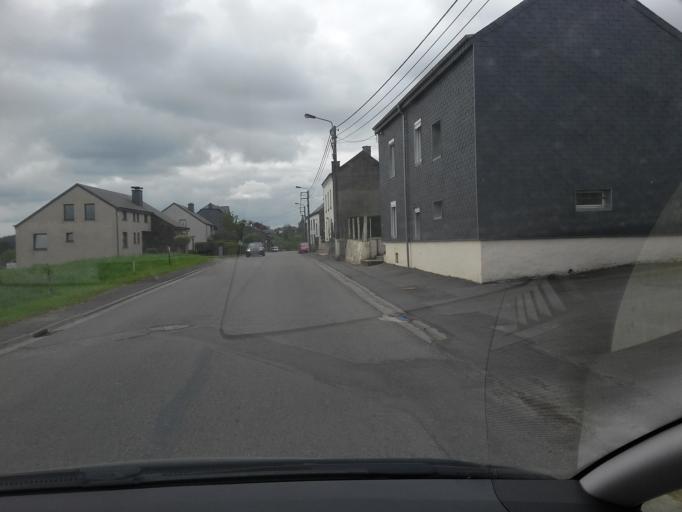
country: BE
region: Wallonia
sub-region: Province du Luxembourg
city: Bertrix
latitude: 49.8244
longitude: 5.3220
